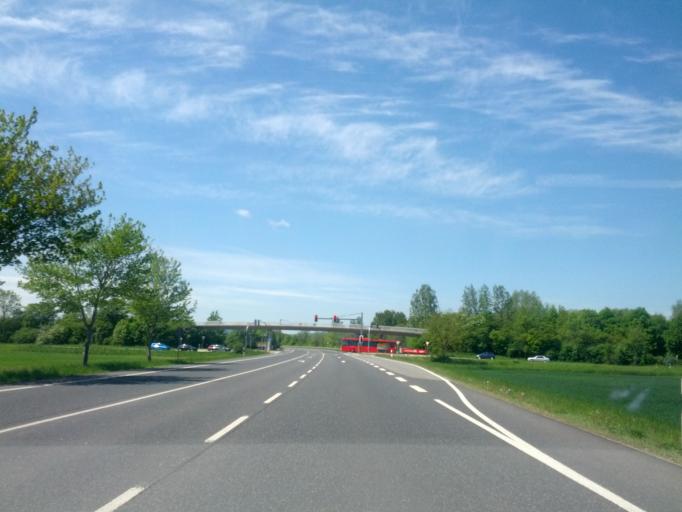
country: DE
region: Hesse
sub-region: Regierungsbezirk Kassel
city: Eschwege
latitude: 51.1984
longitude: 10.0611
